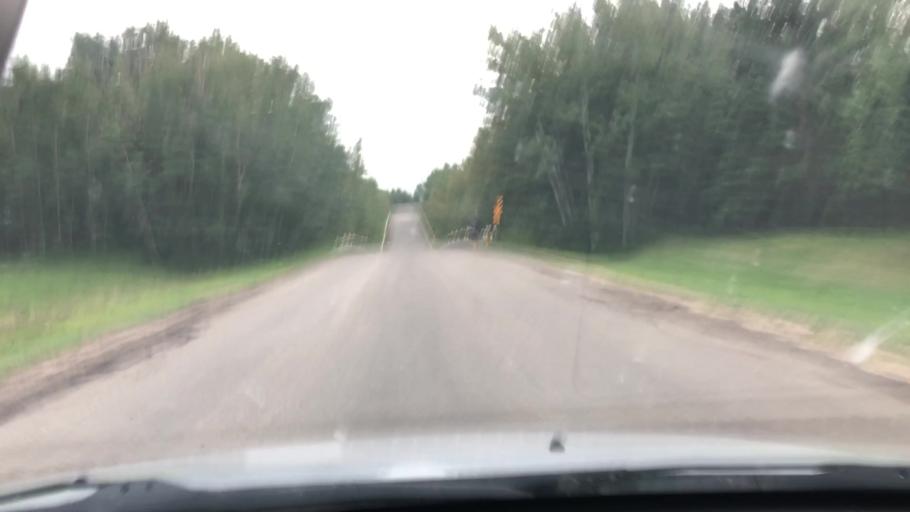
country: CA
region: Alberta
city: Devon
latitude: 53.4284
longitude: -113.6769
